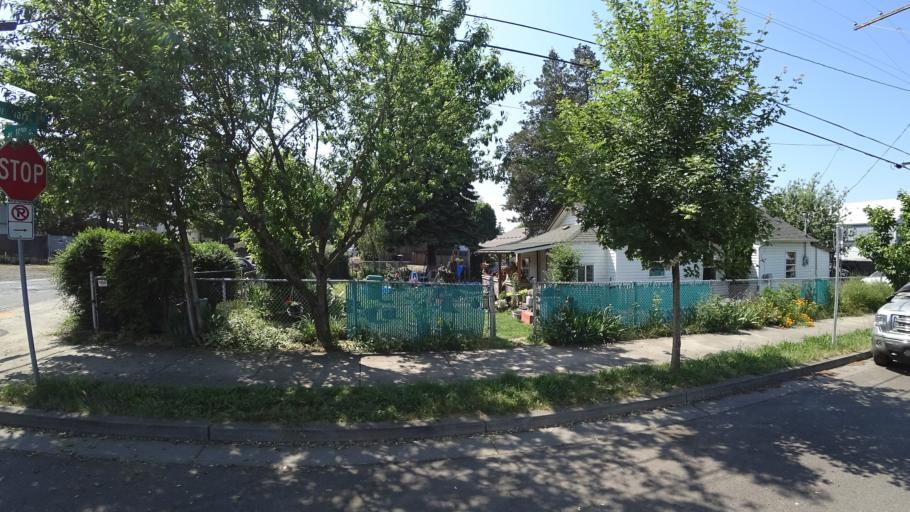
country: US
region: Oregon
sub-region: Multnomah County
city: Lents
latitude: 45.5611
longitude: -122.5507
